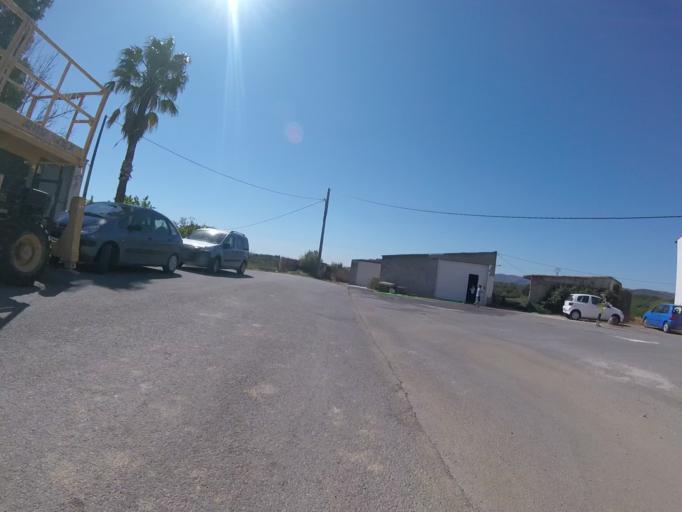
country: ES
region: Valencia
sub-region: Provincia de Castello
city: Cuevas de Vinroma
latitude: 40.3770
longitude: 0.1336
